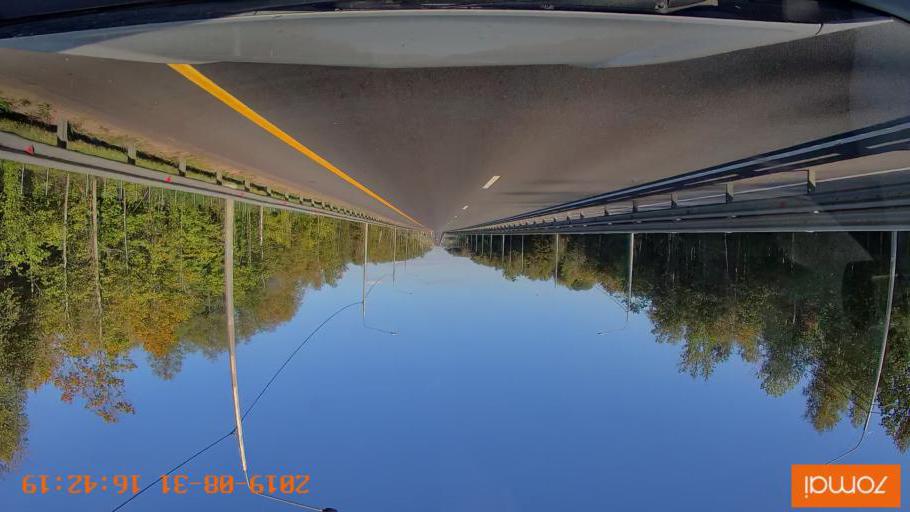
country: RU
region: Kaluga
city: Mstikhino
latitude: 54.5924
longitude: 36.0830
